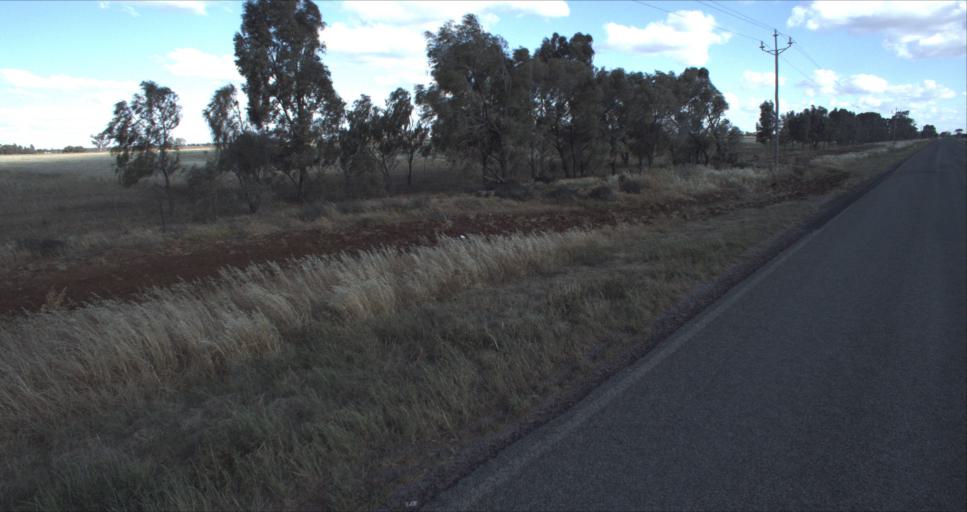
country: AU
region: New South Wales
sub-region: Leeton
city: Leeton
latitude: -34.5308
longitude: 146.2815
